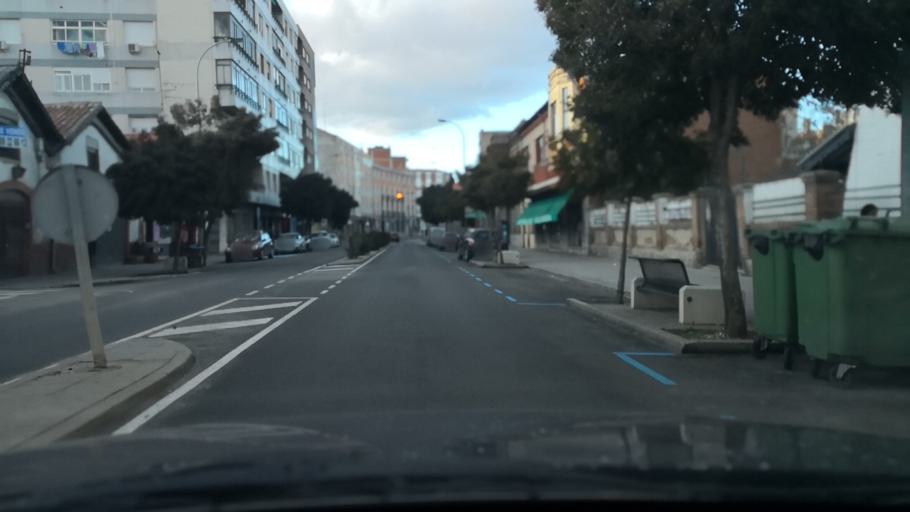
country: ES
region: Castille and Leon
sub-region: Provincia de Valladolid
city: Medina del Campo
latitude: 41.3093
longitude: -4.9127
